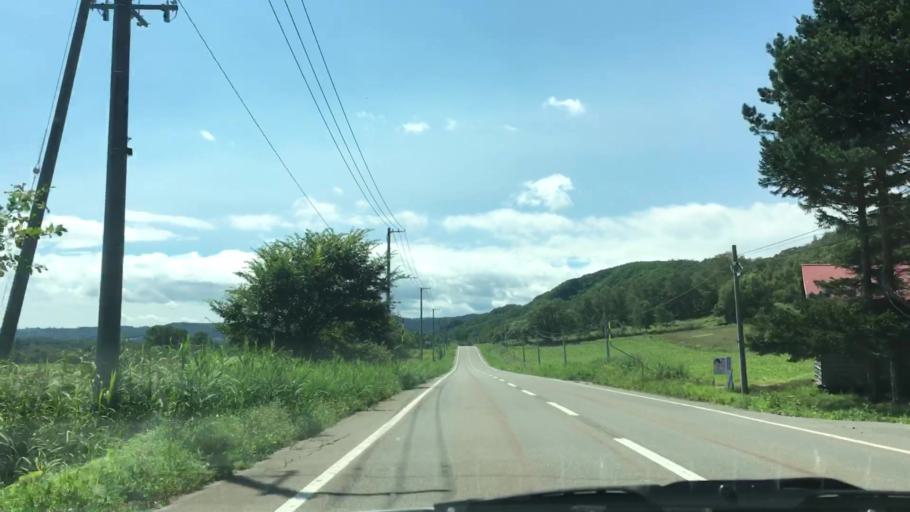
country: JP
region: Hokkaido
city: Otofuke
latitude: 43.2612
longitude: 143.5760
